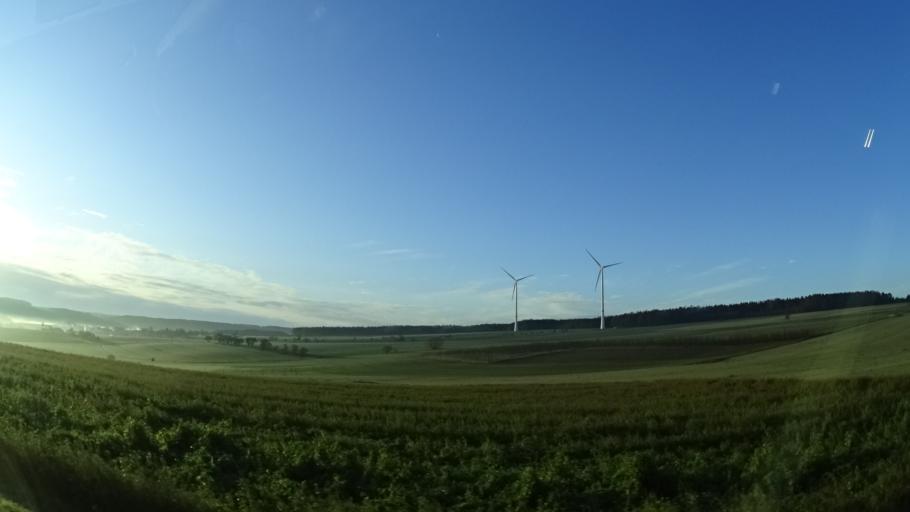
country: DE
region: Bavaria
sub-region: Regierungsbezirk Unterfranken
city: Eichenbuhl
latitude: 49.6679
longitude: 9.3361
